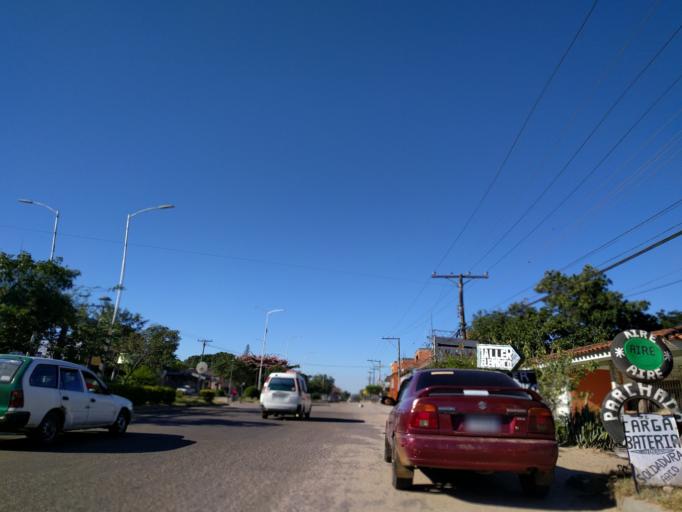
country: BO
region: Santa Cruz
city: Santa Cruz de la Sierra
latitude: -17.8485
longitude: -63.2494
